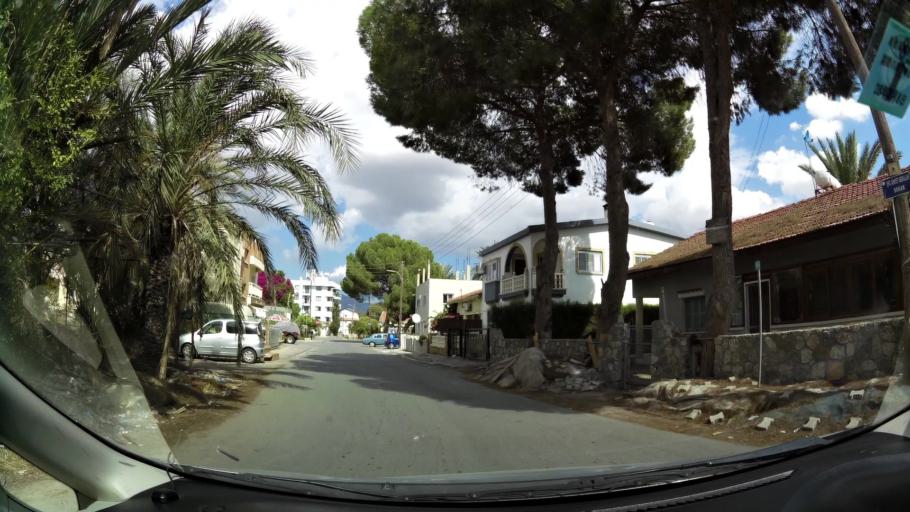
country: CY
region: Lefkosia
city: Nicosia
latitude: 35.1970
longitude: 33.3494
